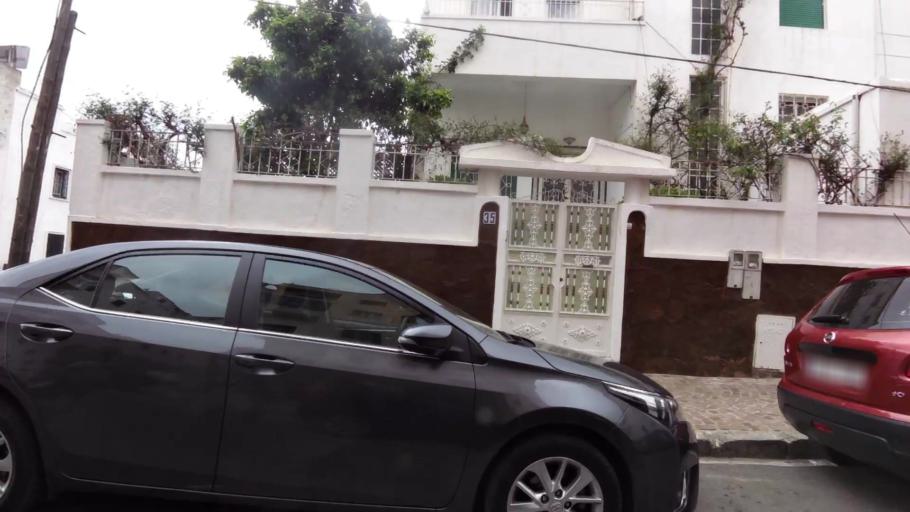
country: MA
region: Tanger-Tetouan
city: Tetouan
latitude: 35.5696
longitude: -5.3785
